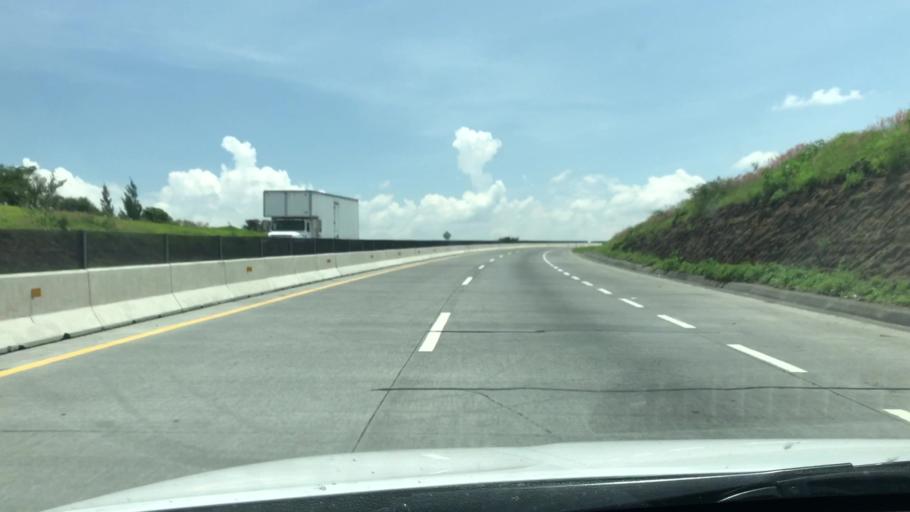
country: MX
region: Jalisco
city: Degollado
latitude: 20.3826
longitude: -102.1191
